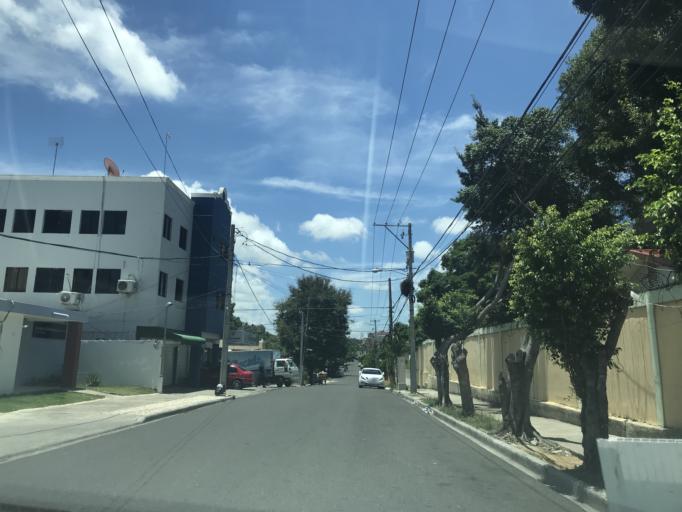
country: DO
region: Santiago
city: Santiago de los Caballeros
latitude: 19.4427
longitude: -70.6987
